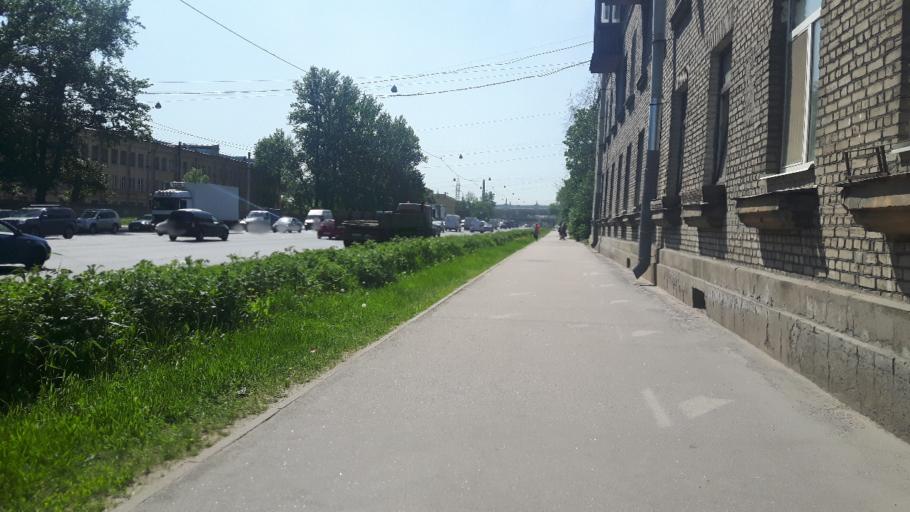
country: RU
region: St.-Petersburg
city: Avtovo
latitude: 59.8884
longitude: 30.2763
